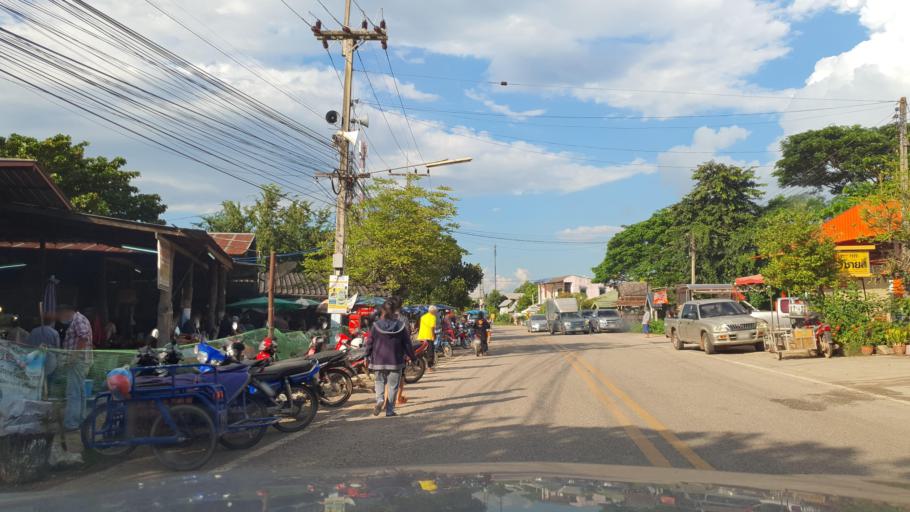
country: TH
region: Phayao
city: Phayao
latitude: 19.1706
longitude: 99.8333
